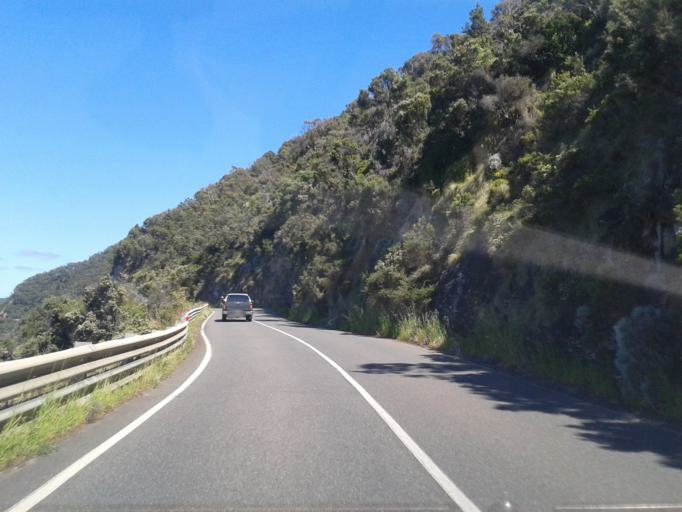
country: AU
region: Victoria
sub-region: Surf Coast
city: Anglesea
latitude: -38.5806
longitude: 143.9442
